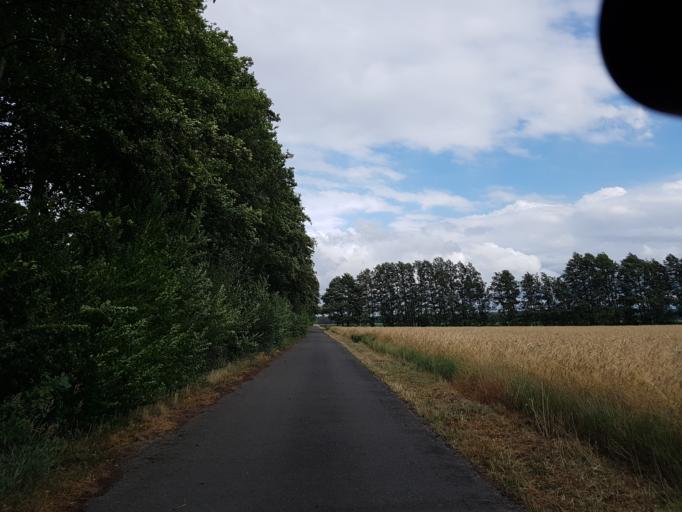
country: DE
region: Saxony-Anhalt
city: Jessen
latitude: 51.8351
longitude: 12.9492
